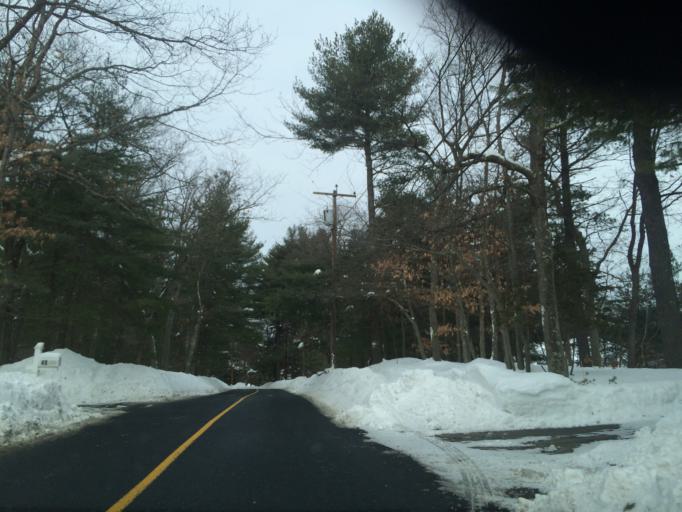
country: US
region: Massachusetts
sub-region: Middlesex County
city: Weston
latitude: 42.3429
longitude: -71.2961
